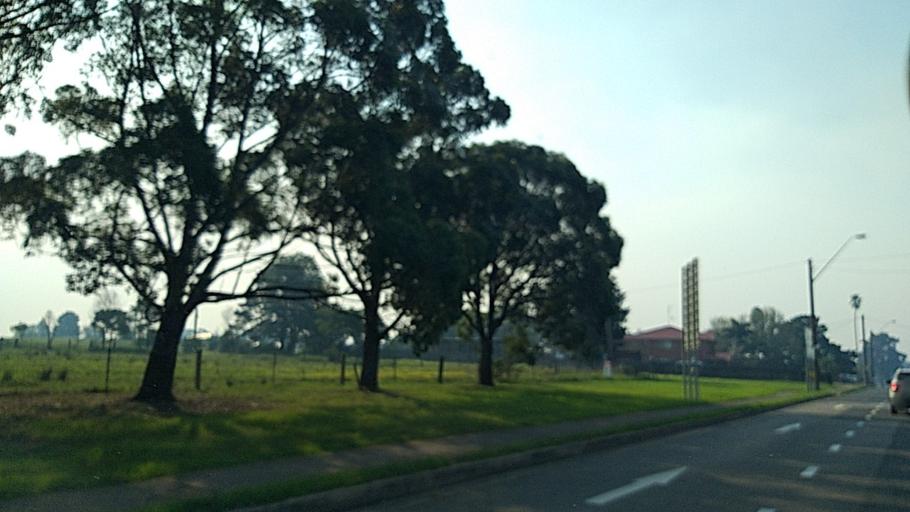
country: AU
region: New South Wales
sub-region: Wollondilly
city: Douglas Park
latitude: -34.2038
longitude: 150.7862
